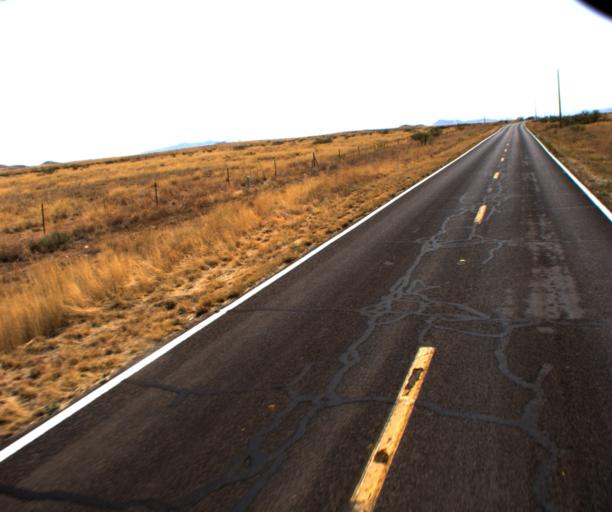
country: US
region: Arizona
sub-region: Cochise County
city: Willcox
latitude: 31.9861
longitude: -109.4553
